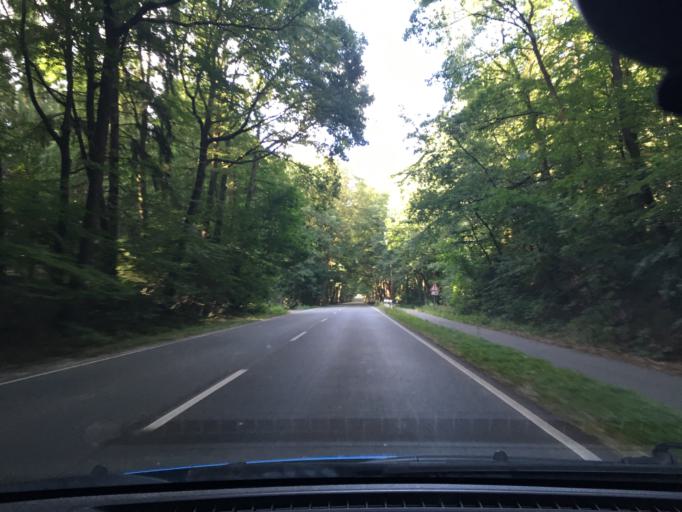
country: DE
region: Lower Saxony
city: Seevetal
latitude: 53.4150
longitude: 9.9279
